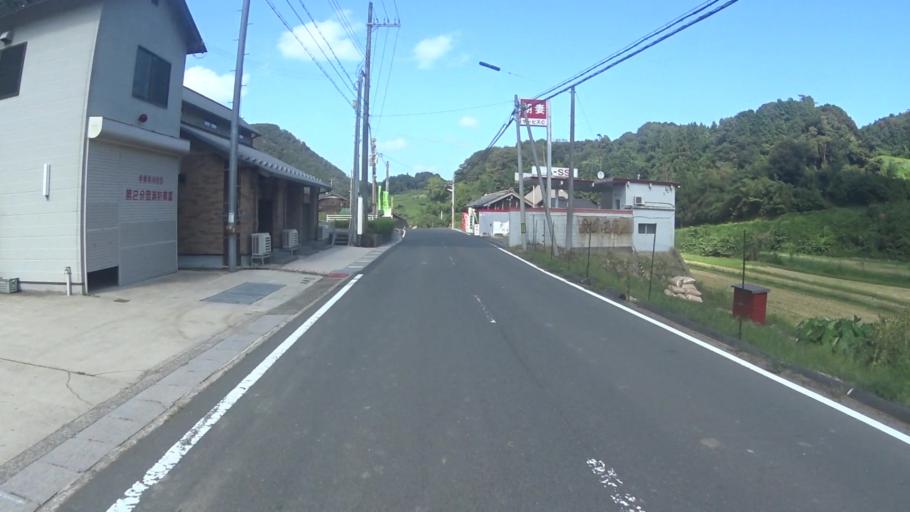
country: JP
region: Kyoto
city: Miyazu
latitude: 35.6954
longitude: 135.2777
